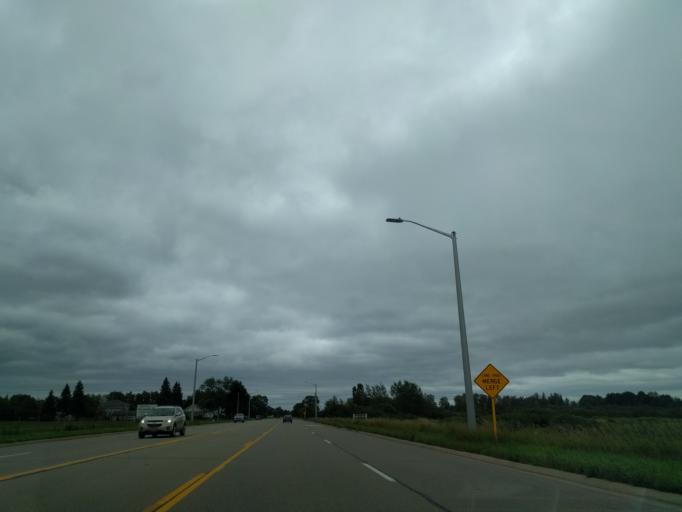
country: US
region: Michigan
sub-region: Delta County
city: Escanaba
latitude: 45.7268
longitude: -87.0800
